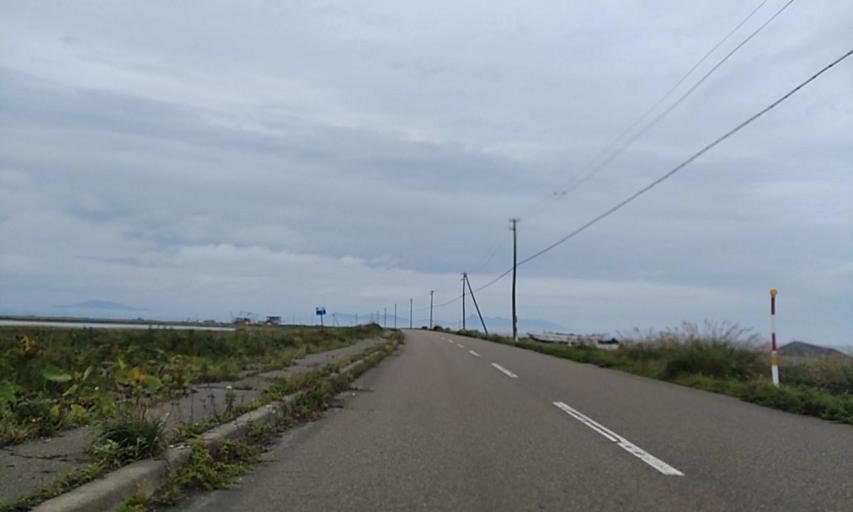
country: JP
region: Hokkaido
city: Shibetsu
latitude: 43.5841
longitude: 145.3419
